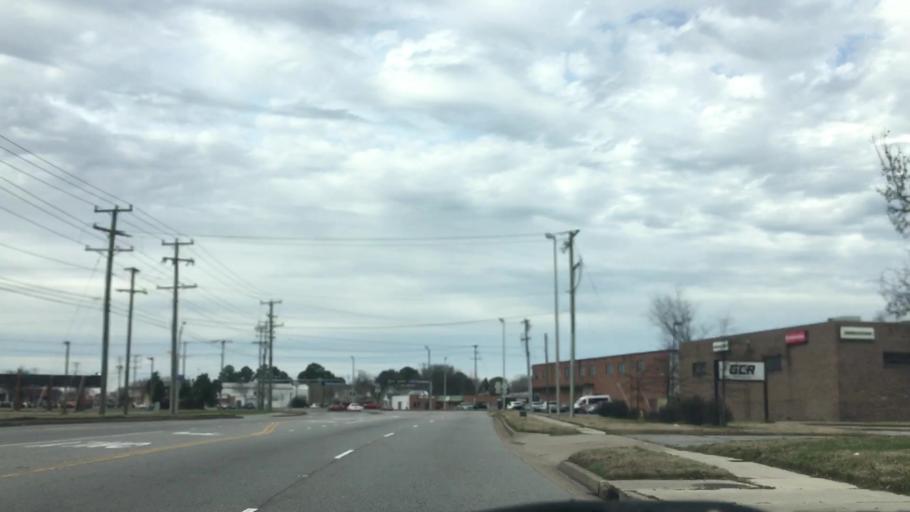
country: US
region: Virginia
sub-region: City of Norfolk
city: Norfolk
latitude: 36.8614
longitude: -76.2435
